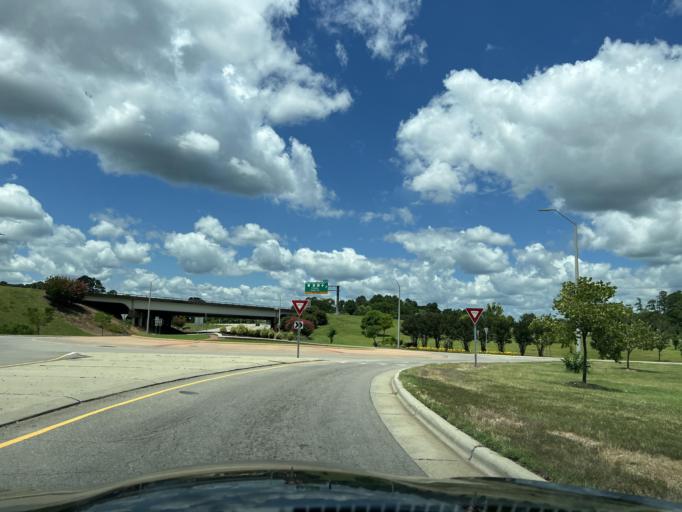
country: US
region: North Carolina
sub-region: Lee County
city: Sanford
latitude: 35.5221
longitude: -79.1830
